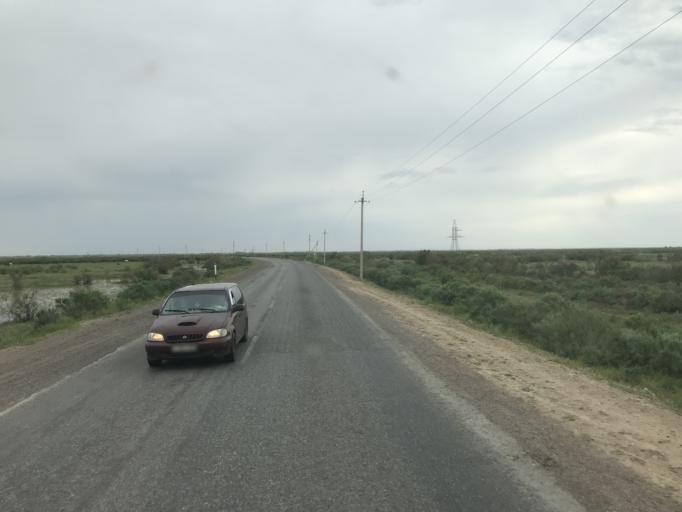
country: KZ
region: Ongtustik Qazaqstan
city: Asykata
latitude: 41.0069
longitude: 68.4760
